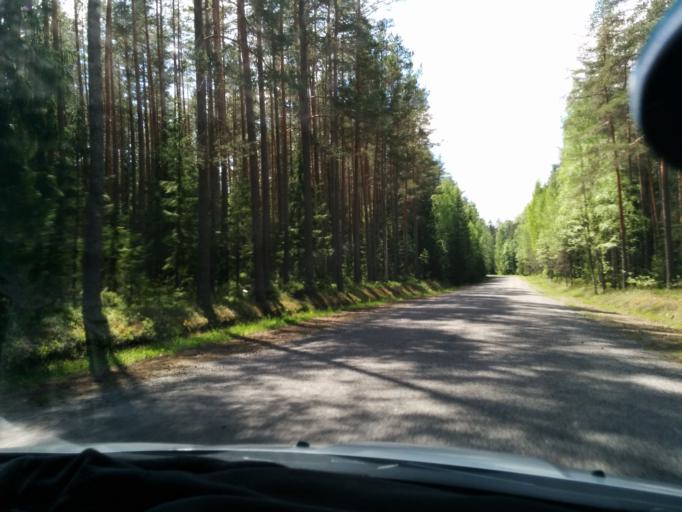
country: EE
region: Harju
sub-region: Loksa linn
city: Loksa
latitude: 59.5253
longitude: 25.9613
